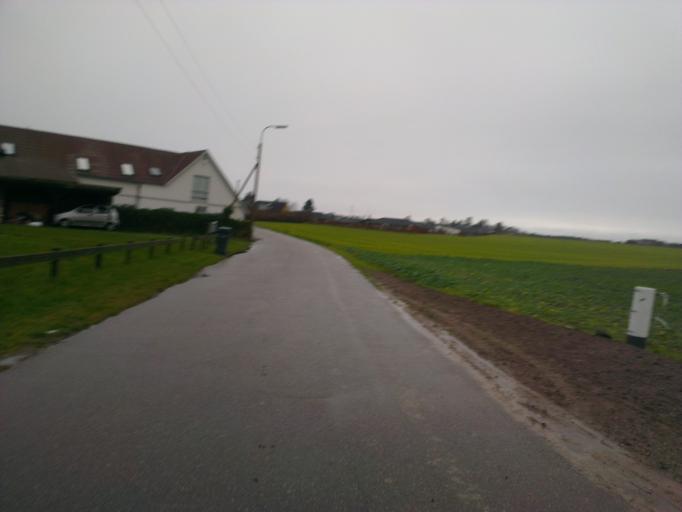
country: DK
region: Capital Region
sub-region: Frederikssund Kommune
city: Jaegerspris
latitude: 55.8328
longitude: 11.9963
